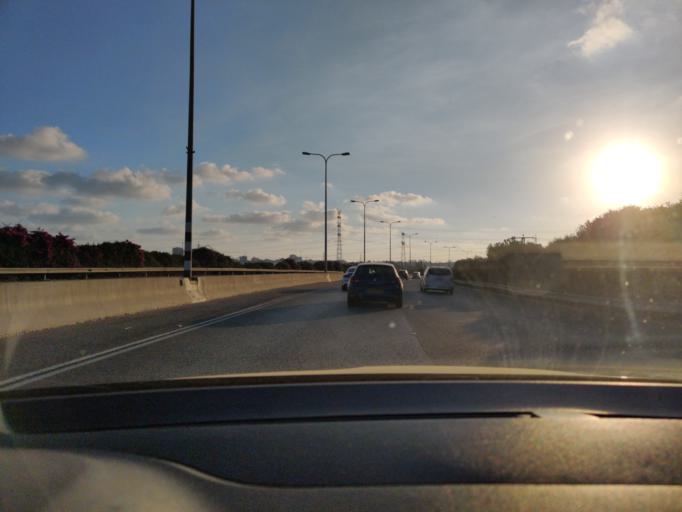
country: IL
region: Haifa
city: Hadera
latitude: 32.4463
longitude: 34.9491
